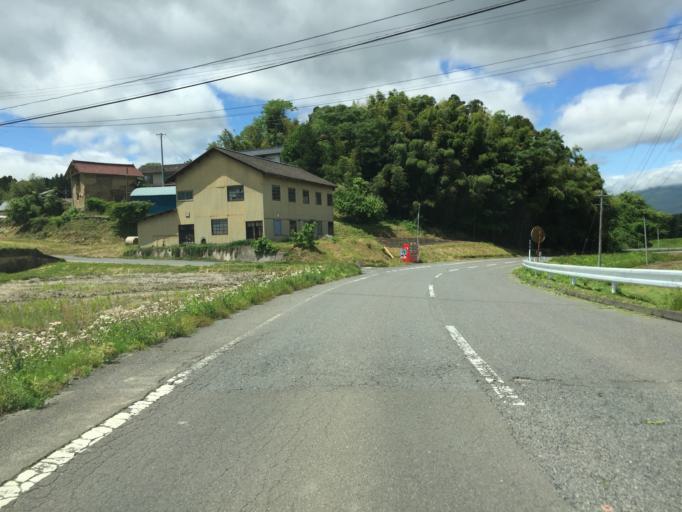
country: JP
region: Fukushima
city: Nihommatsu
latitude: 37.5235
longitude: 140.4714
